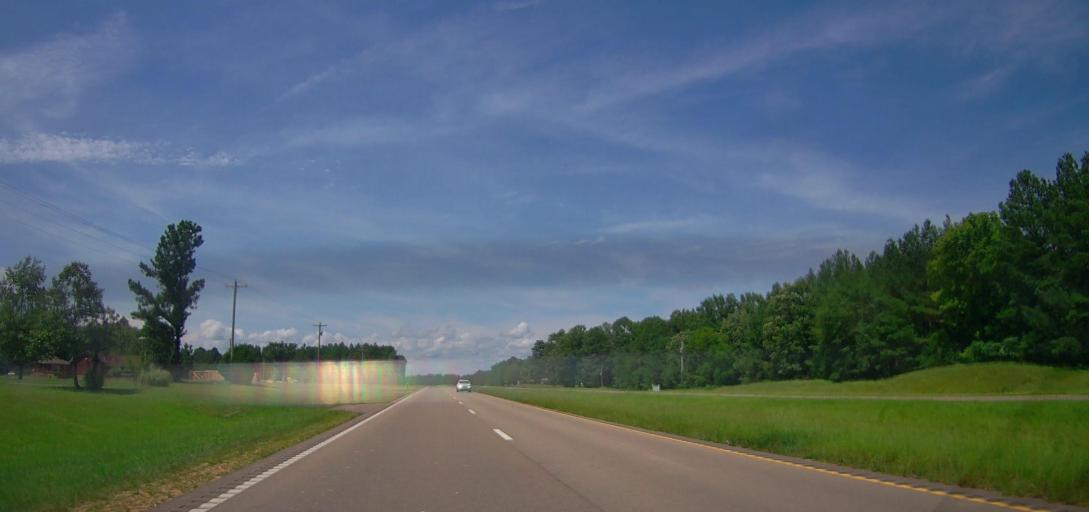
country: US
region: Mississippi
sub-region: Monroe County
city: Aberdeen
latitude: 33.9229
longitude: -88.5962
